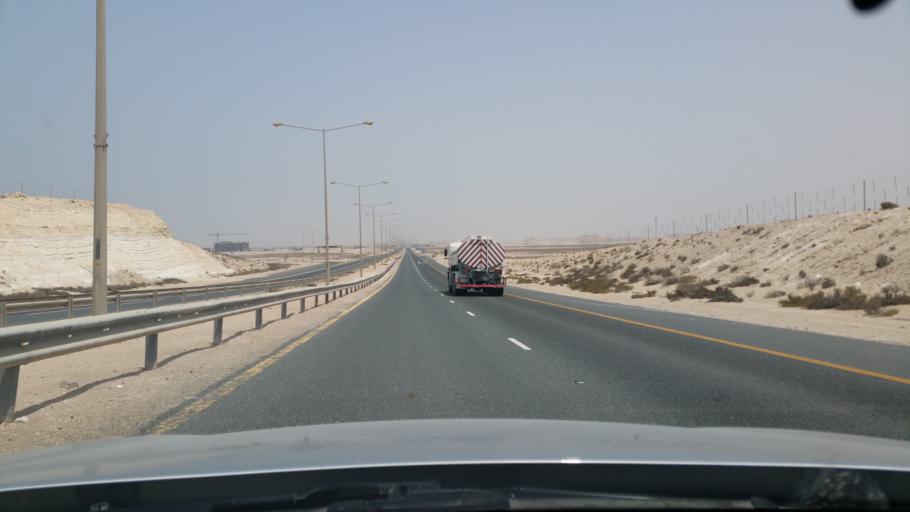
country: QA
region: Baladiyat ar Rayyan
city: Dukhan
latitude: 25.3628
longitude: 50.7796
